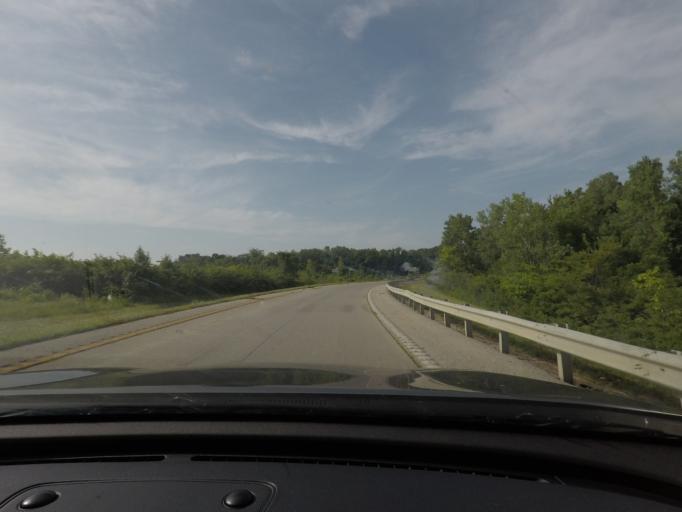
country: US
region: Missouri
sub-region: Saint Louis County
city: Bridgeton
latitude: 38.7709
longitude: -90.4088
